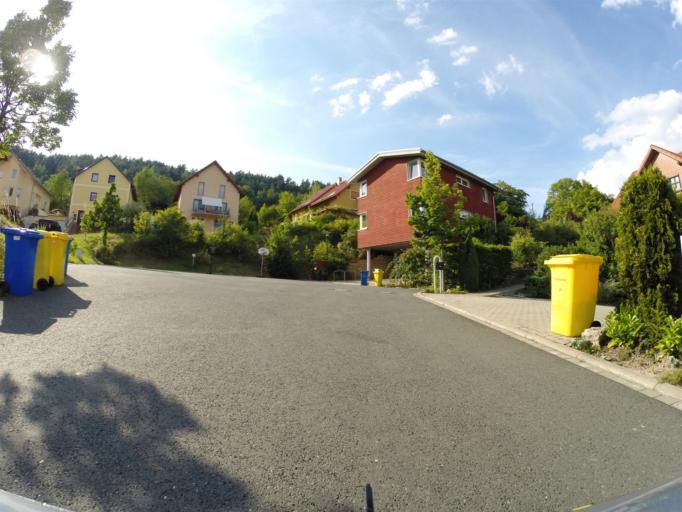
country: DE
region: Thuringia
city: Neuengonna
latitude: 50.9668
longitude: 11.6222
